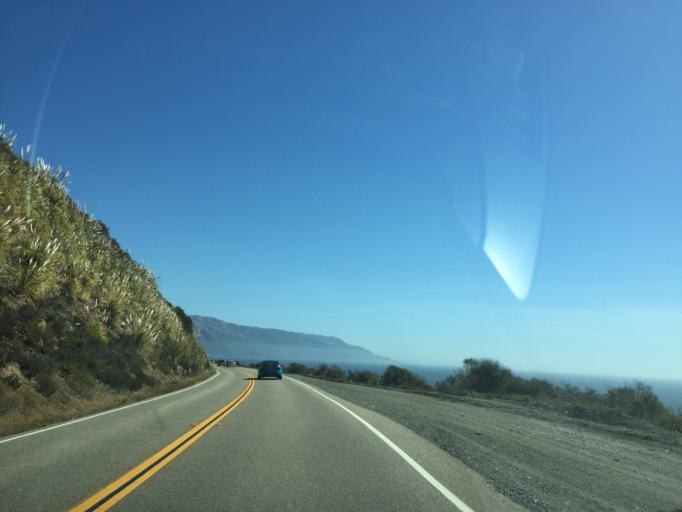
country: US
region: California
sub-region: Monterey County
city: Greenfield
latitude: 36.0243
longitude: -121.5711
